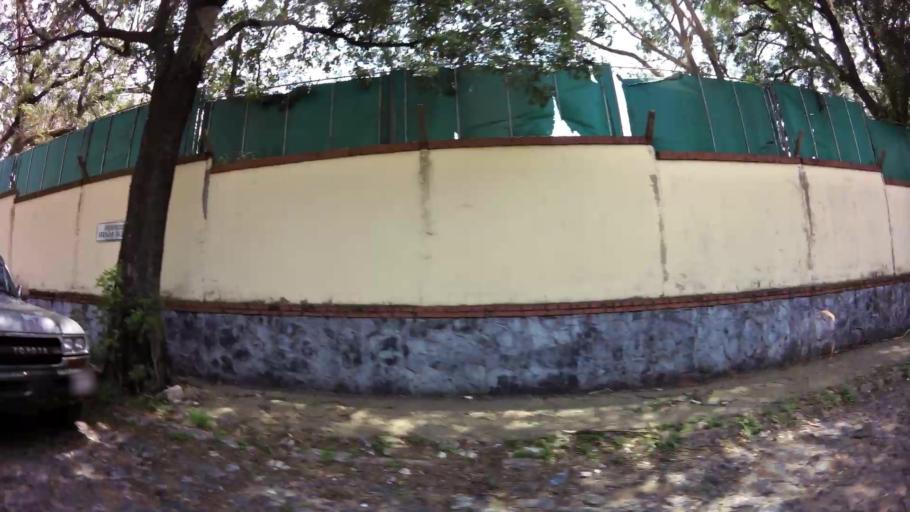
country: PY
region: Asuncion
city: Asuncion
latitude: -25.2976
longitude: -57.6035
